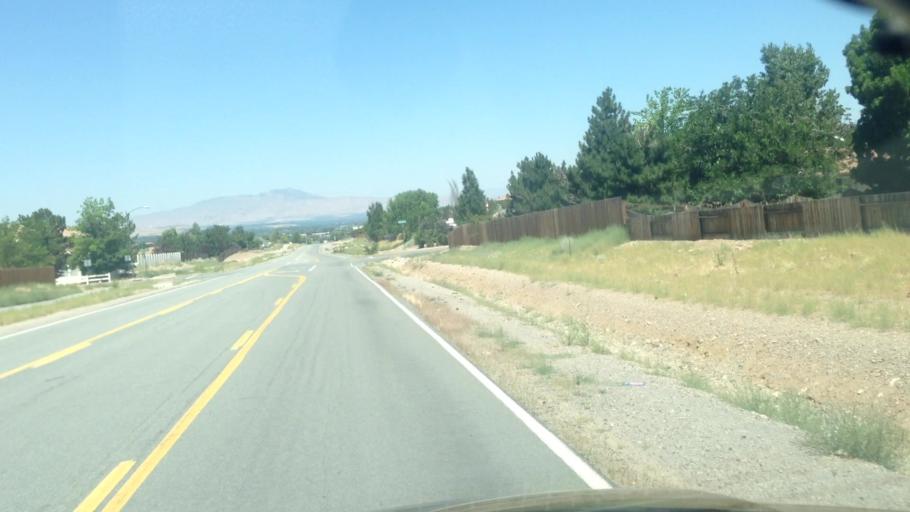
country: US
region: Nevada
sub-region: Storey County
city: Virginia City
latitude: 39.3871
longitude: -119.7269
